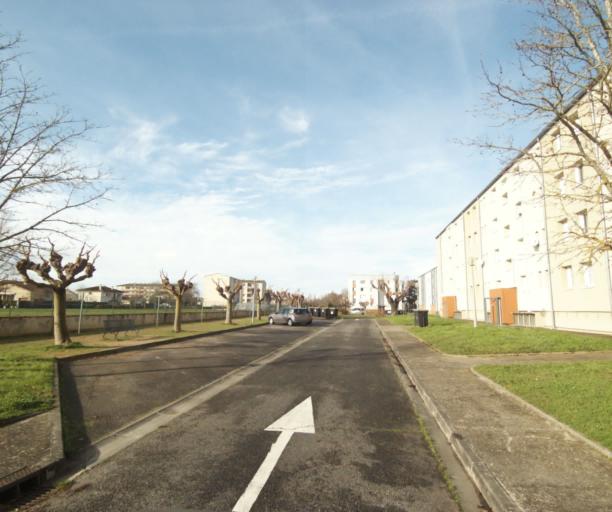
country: FR
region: Midi-Pyrenees
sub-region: Departement de la Haute-Garonne
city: Villemur-sur-Tarn
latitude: 43.8624
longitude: 1.4991
